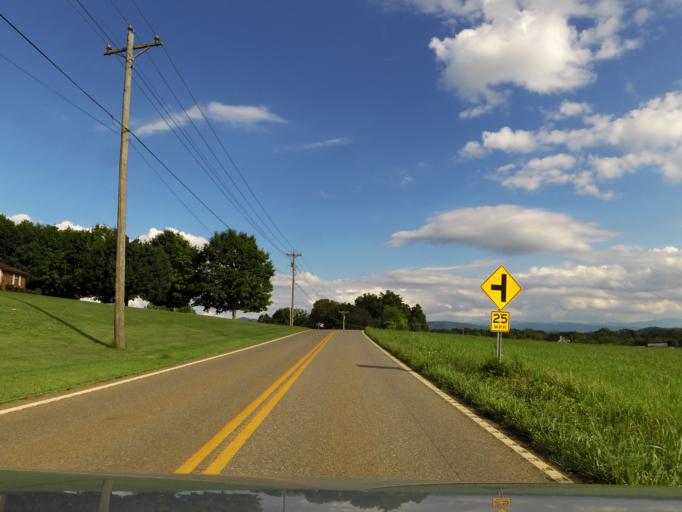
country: US
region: Tennessee
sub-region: Loudon County
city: Greenback
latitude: 35.6432
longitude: -84.1016
